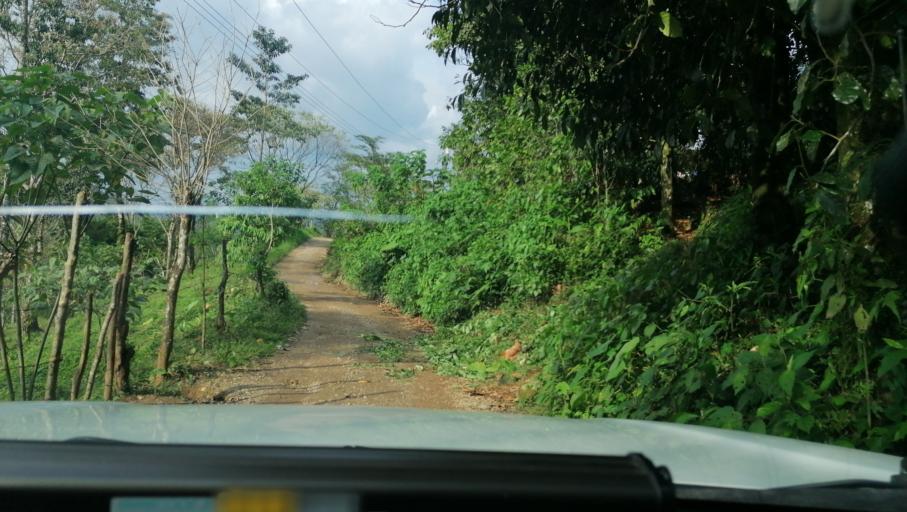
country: MX
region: Chiapas
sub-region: Tapilula
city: San Francisco Jacona
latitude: 17.3295
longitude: -93.1015
